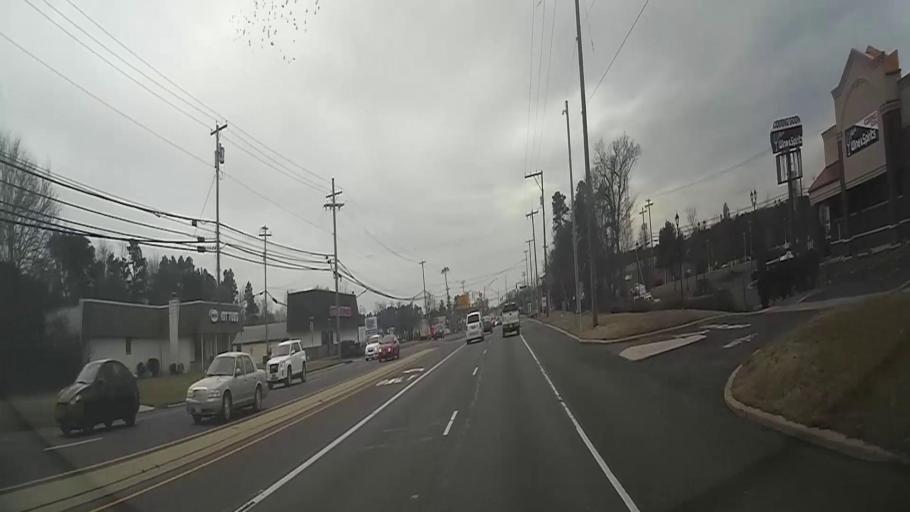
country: US
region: New Jersey
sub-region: Camden County
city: Berlin
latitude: 39.8263
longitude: -74.9277
